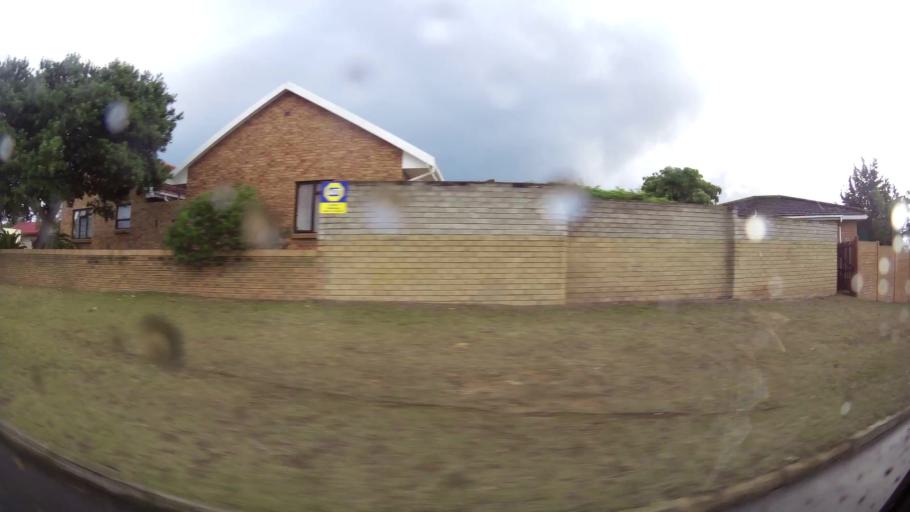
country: ZA
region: Western Cape
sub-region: Eden District Municipality
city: Mossel Bay
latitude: -34.1892
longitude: 22.1140
